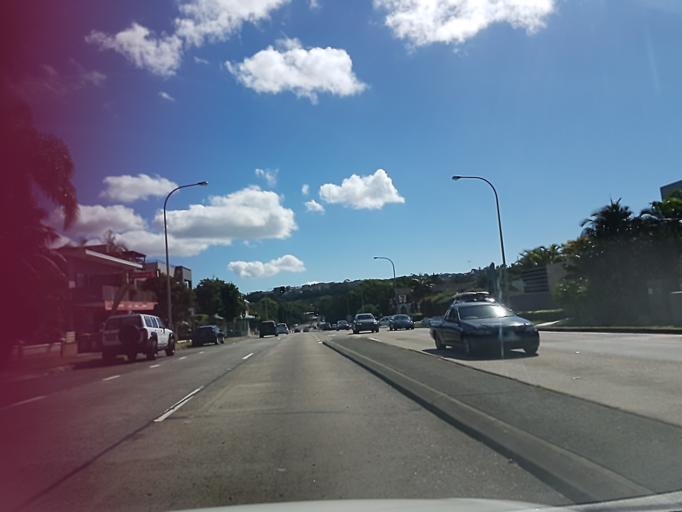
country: AU
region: New South Wales
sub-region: Warringah
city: Dee Why
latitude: -33.7501
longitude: 151.2893
